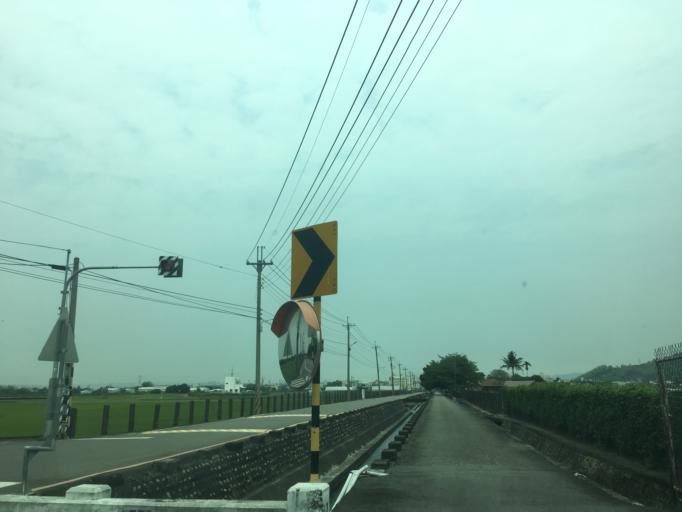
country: TW
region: Taiwan
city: Zhongxing New Village
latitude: 24.0296
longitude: 120.6887
